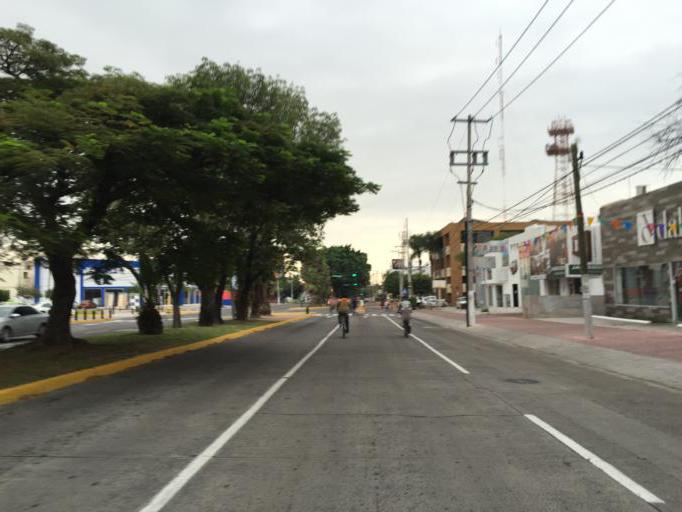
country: MX
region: Jalisco
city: Guadalajara
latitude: 20.6666
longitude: -103.3771
